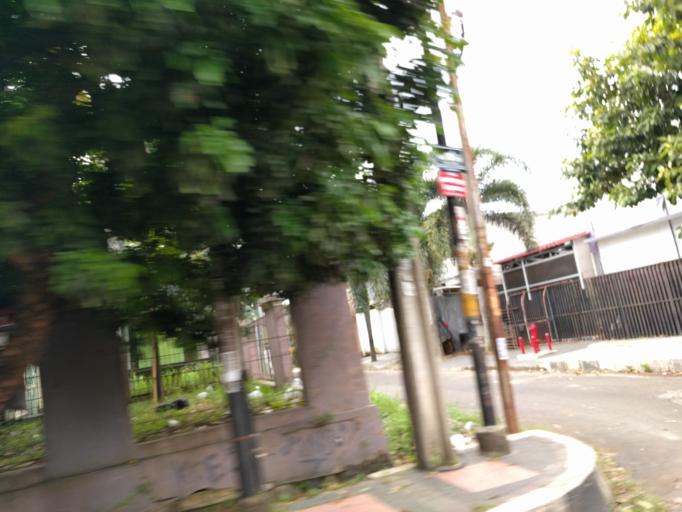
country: ID
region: West Java
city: Bogor
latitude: -6.5850
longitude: 106.8168
